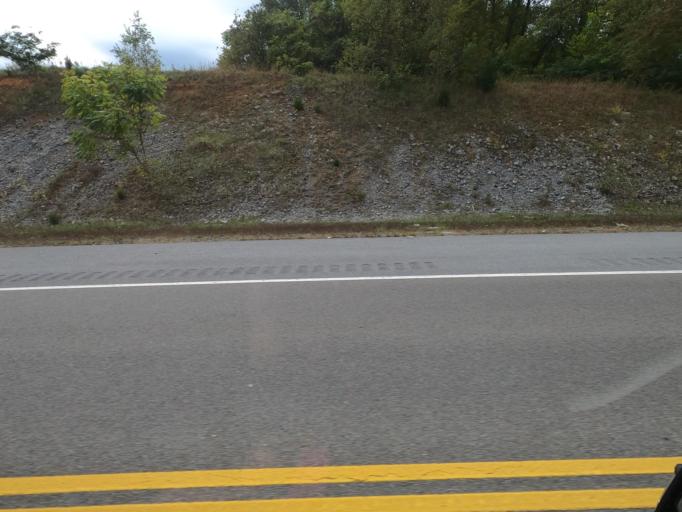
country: US
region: Tennessee
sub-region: Carter County
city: Central
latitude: 36.3158
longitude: -82.2486
